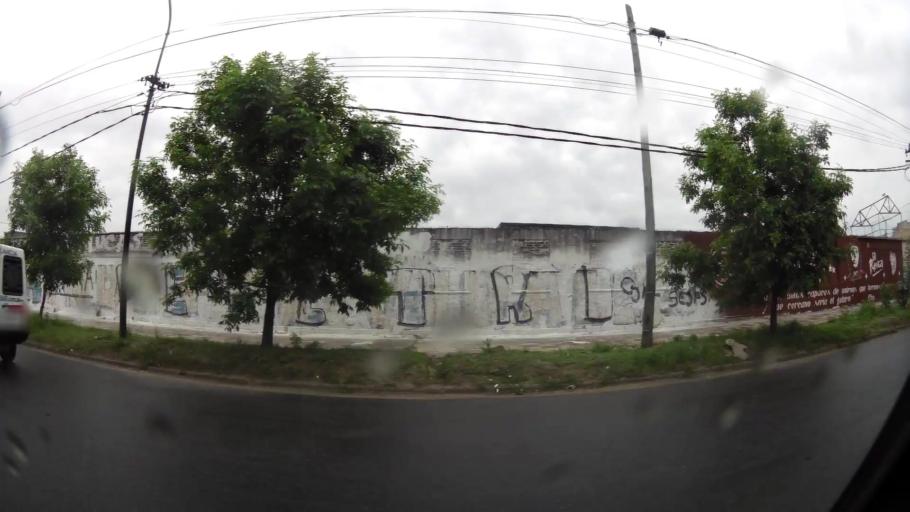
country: AR
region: Buenos Aires
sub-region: Partido de Lanus
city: Lanus
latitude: -34.6829
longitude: -58.4048
